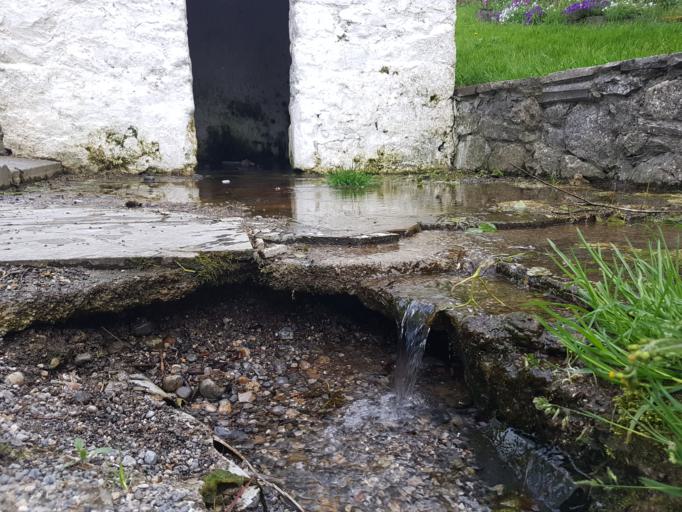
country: IE
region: Leinster
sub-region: Kilkenny
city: Kilkenny
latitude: 52.6533
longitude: -7.2621
